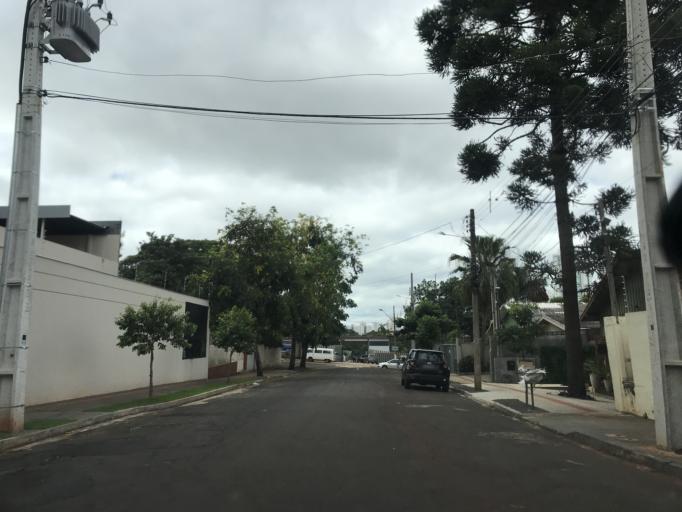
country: BR
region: Parana
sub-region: Londrina
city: Londrina
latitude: -23.3232
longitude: -51.1706
